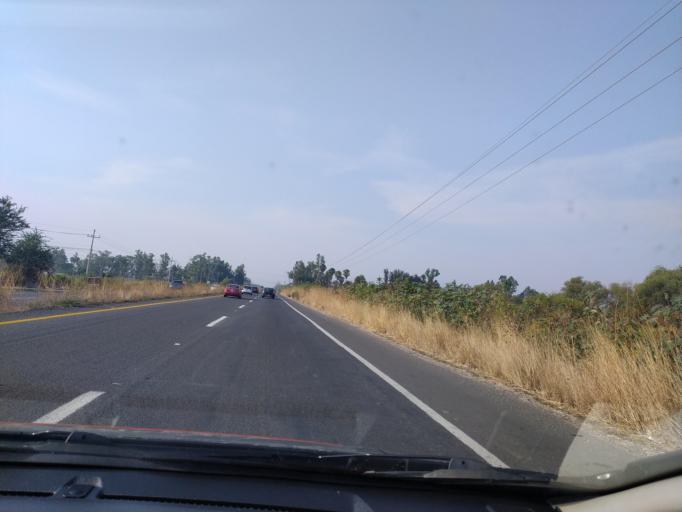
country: MX
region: Jalisco
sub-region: Acatlan de Juarez
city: Villa de los Ninos
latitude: 20.3976
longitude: -103.5936
